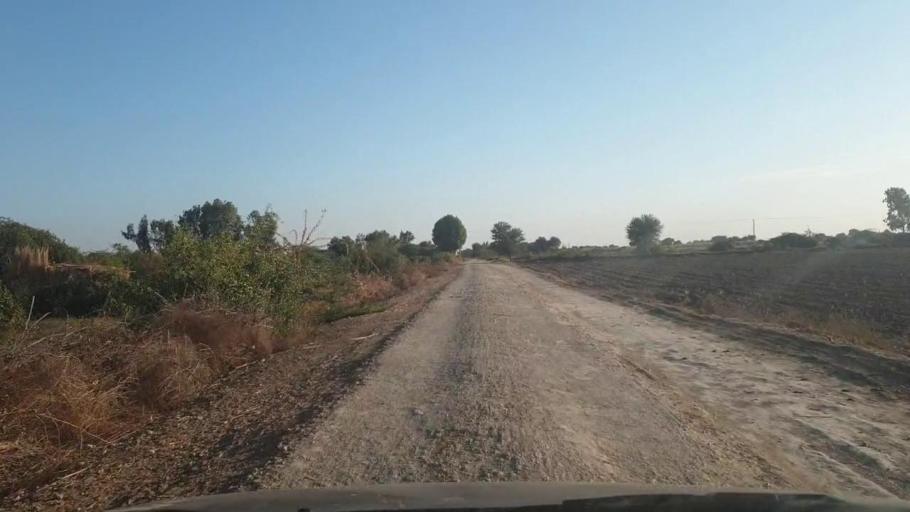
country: PK
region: Sindh
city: Sinjhoro
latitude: 26.0340
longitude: 68.8715
